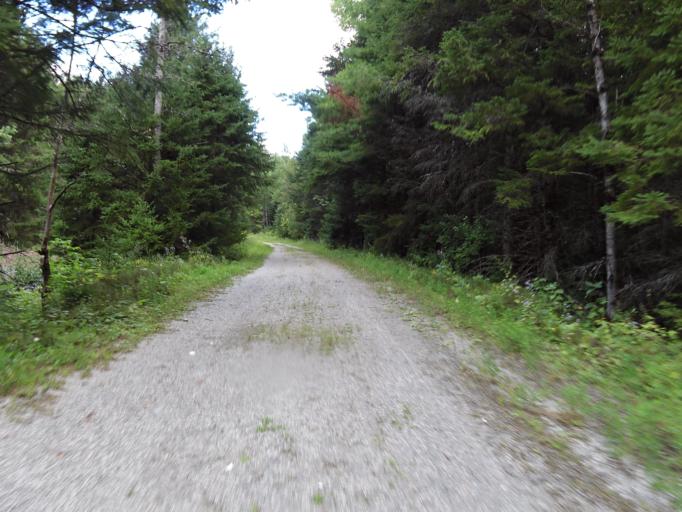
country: CA
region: Quebec
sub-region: Outaouais
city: Wakefield
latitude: 45.8558
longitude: -75.9920
